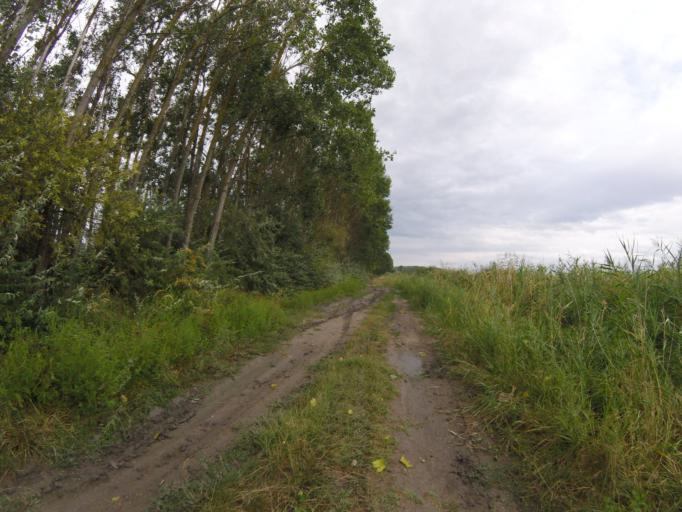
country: HU
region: Gyor-Moson-Sopron
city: Nagycenk
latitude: 47.6350
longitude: 16.7643
